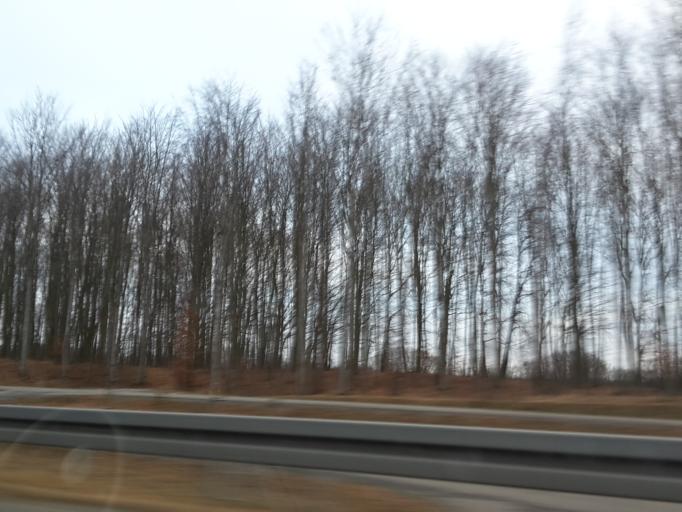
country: PL
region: Warmian-Masurian Voivodeship
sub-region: Powiat ostrodzki
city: Maldyty
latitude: 53.9168
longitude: 19.7229
